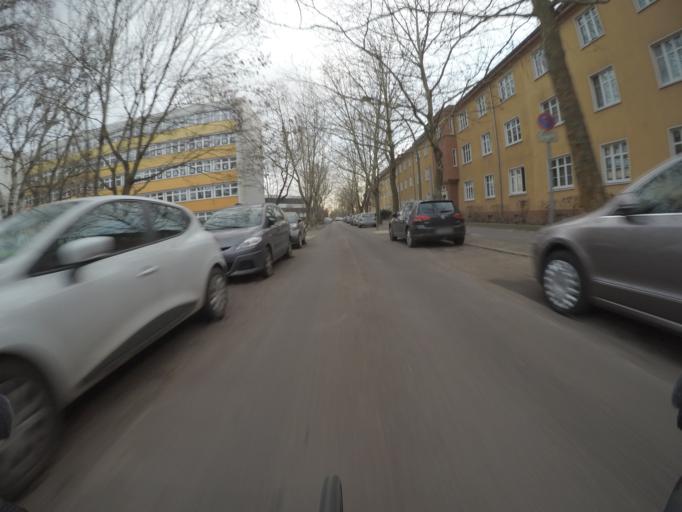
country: DE
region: Berlin
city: Karlshorst
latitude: 52.4792
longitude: 13.5334
